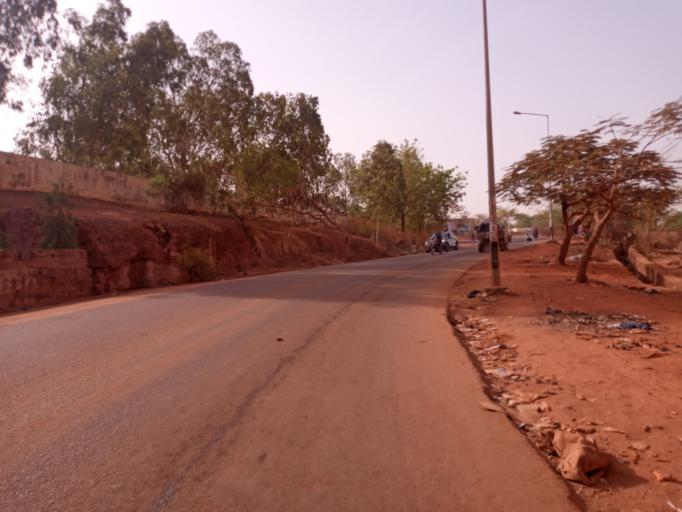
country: ML
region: Bamako
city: Bamako
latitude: 12.6129
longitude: -7.9926
